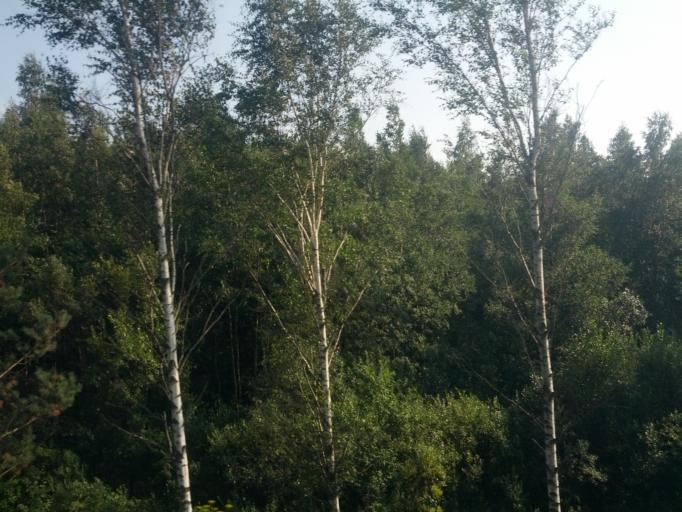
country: RU
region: Leningrad
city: Staraya
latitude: 59.8892
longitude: 30.6277
